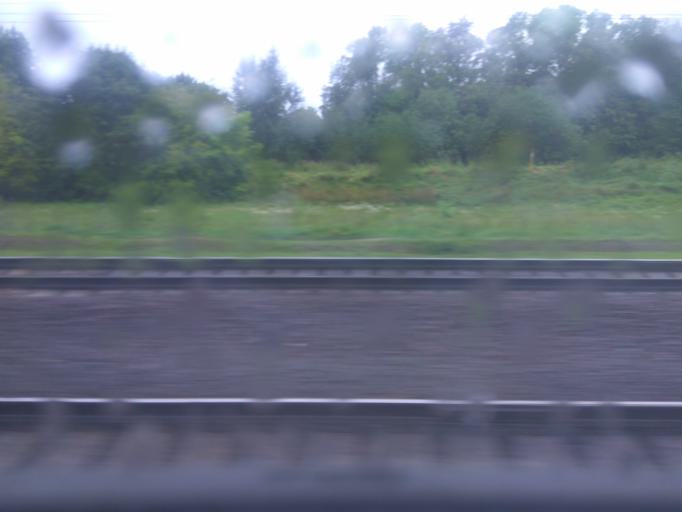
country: RU
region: Moscow
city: Zagor'ye
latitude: 55.5709
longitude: 37.6648
